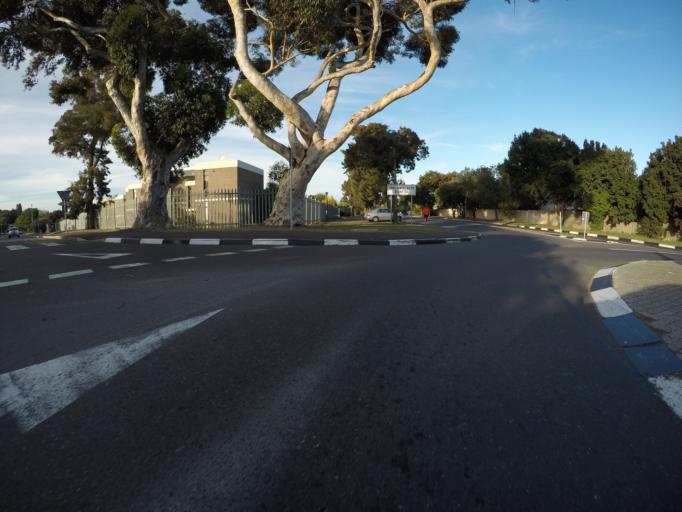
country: ZA
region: Western Cape
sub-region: City of Cape Town
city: Kraaifontein
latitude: -33.8673
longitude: 18.6521
